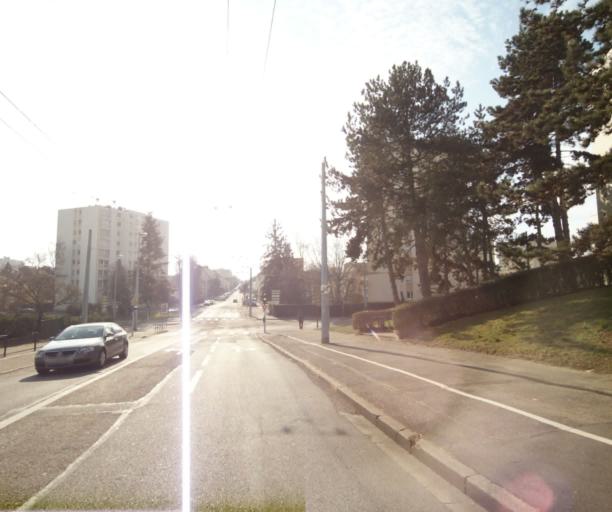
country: FR
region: Lorraine
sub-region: Departement de Meurthe-et-Moselle
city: Laxou
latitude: 48.6807
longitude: 6.1531
